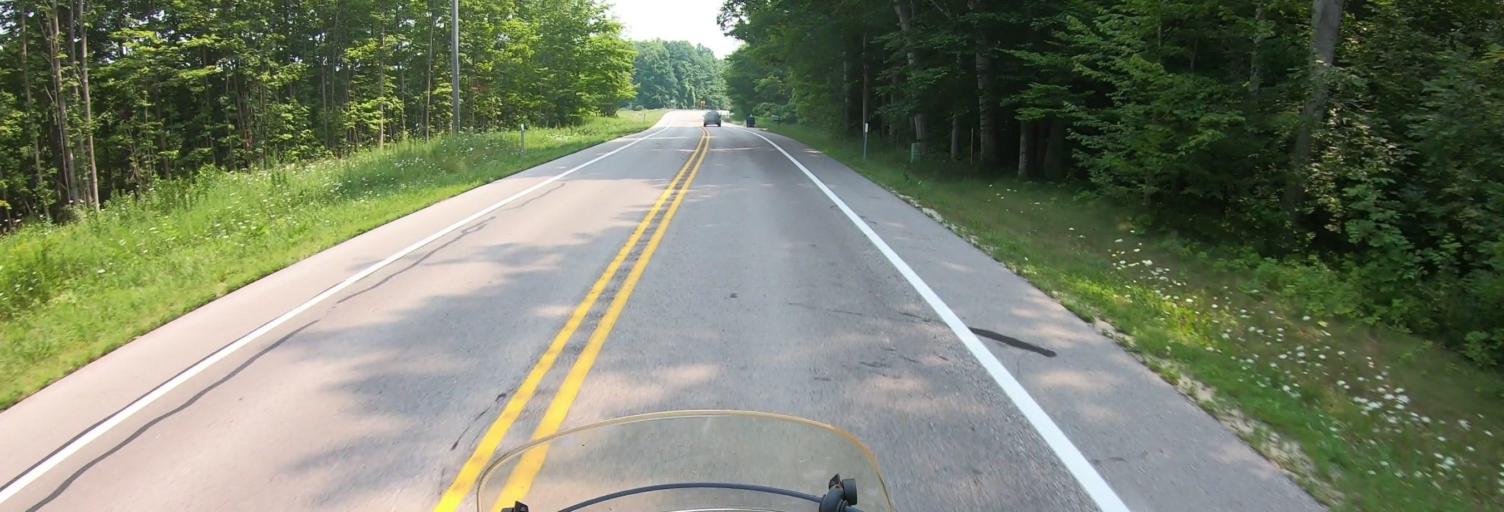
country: US
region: Michigan
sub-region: Leelanau County
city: Leland
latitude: 45.0854
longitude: -85.5977
